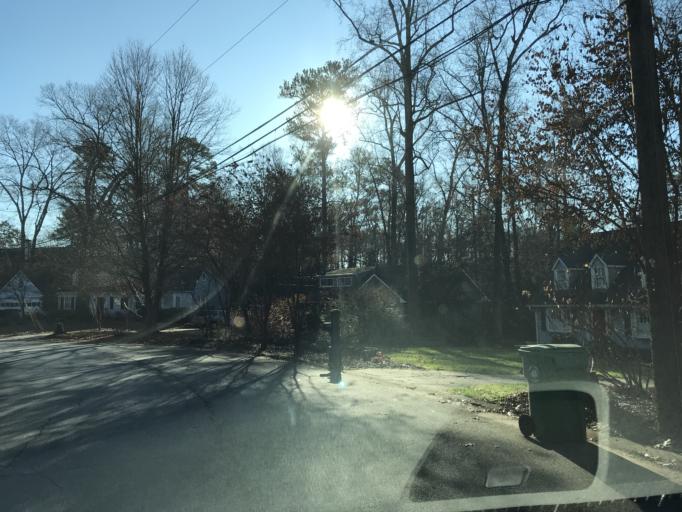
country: US
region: Georgia
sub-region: DeKalb County
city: North Atlanta
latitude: 33.8815
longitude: -84.3379
